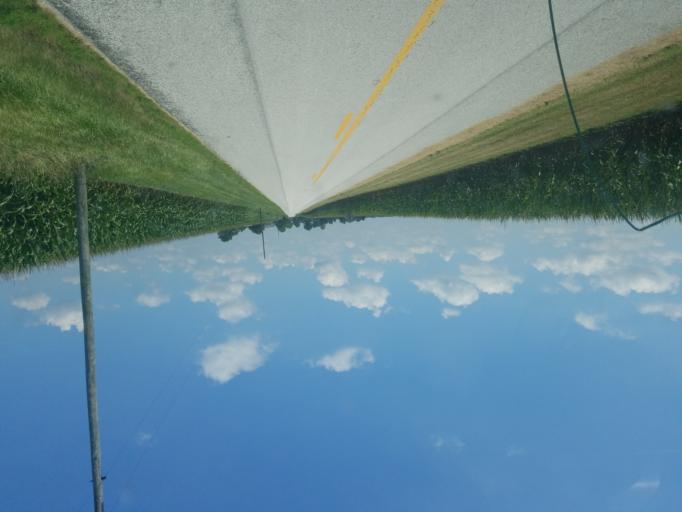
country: US
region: Ohio
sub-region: Allen County
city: Spencerville
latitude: 40.6666
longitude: -84.4216
